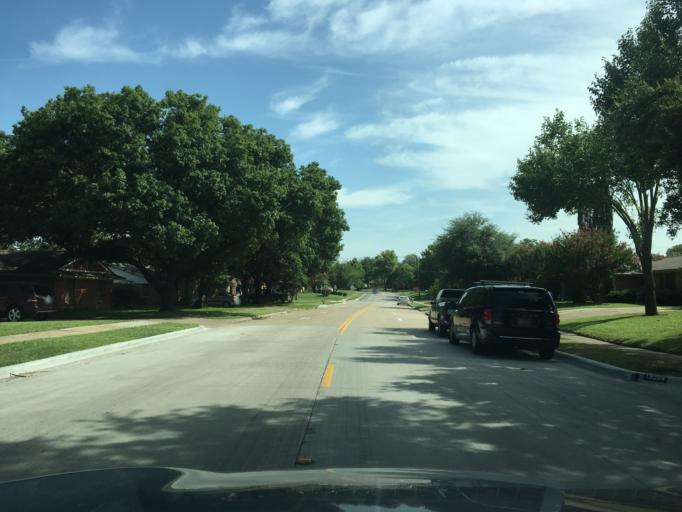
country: US
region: Texas
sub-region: Dallas County
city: Richardson
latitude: 32.9278
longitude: -96.7751
